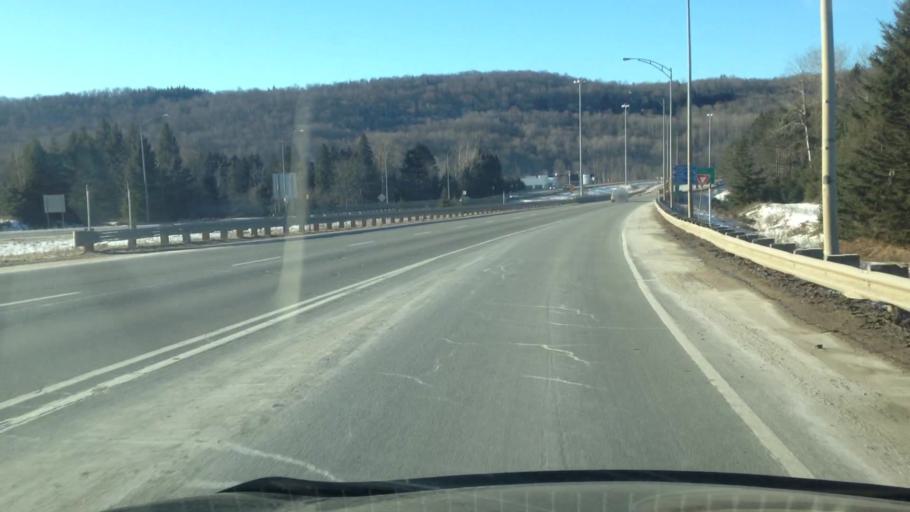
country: CA
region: Quebec
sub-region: Laurentides
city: Mont-Tremblant
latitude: 46.1134
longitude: -74.5994
